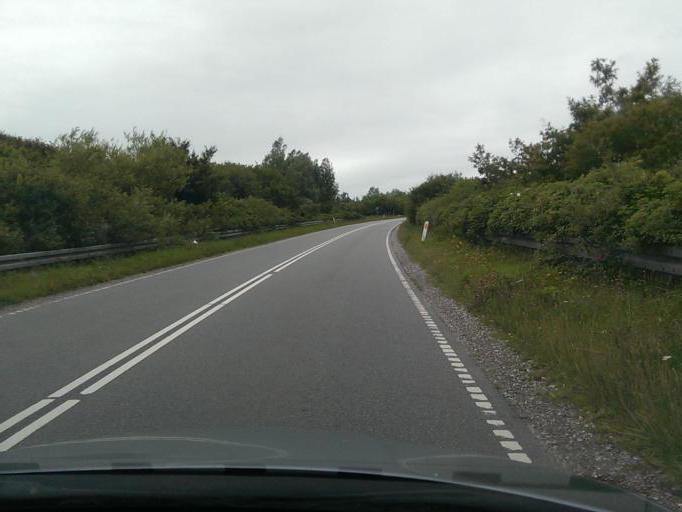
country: DK
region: North Denmark
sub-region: Hjorring Kommune
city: Vra
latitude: 57.3532
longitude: 9.9140
